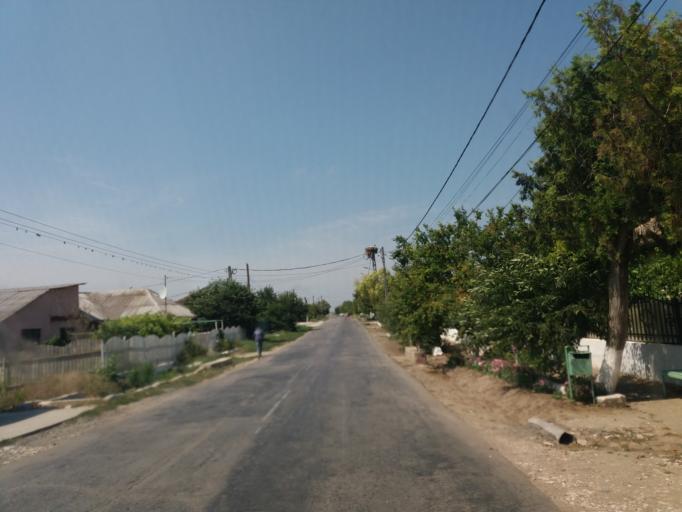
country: RO
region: Constanta
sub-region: Comuna Corbu
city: Corbu
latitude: 44.4194
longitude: 28.6608
